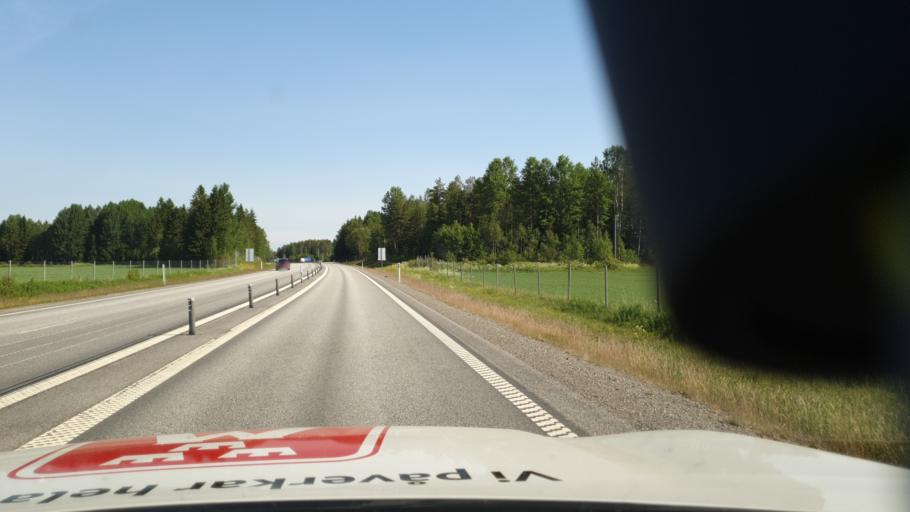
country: SE
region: Vaesterbotten
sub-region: Robertsfors Kommun
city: Robertsfors
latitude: 64.0826
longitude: 20.8676
